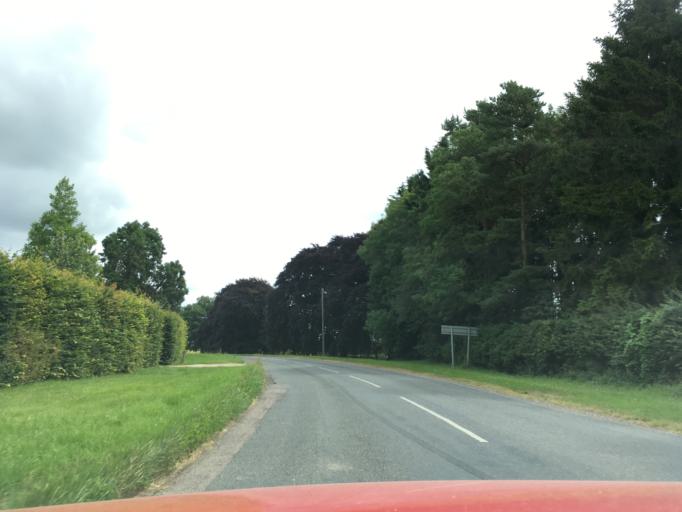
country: GB
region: England
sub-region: Oxfordshire
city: Shipton under Wychwood
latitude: 51.9019
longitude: -1.6095
